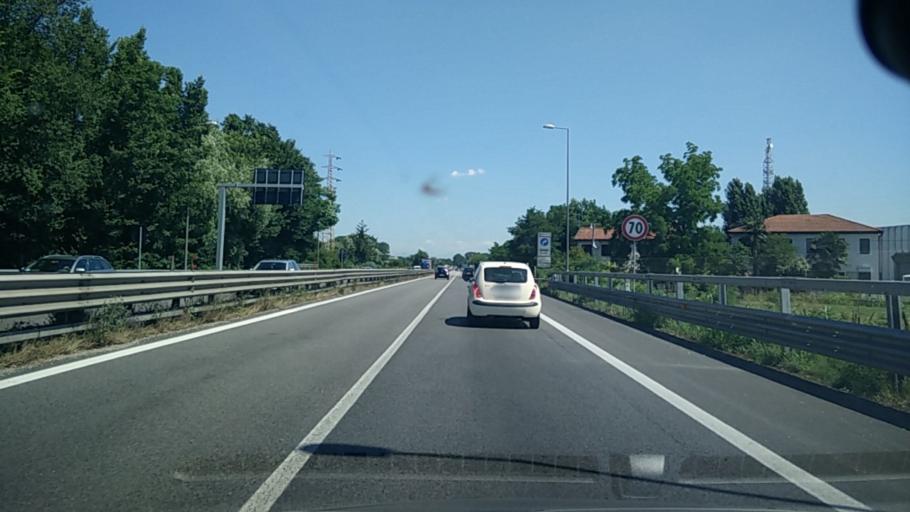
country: IT
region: Veneto
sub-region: Provincia di Venezia
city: Mestre
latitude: 45.4616
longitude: 12.2102
